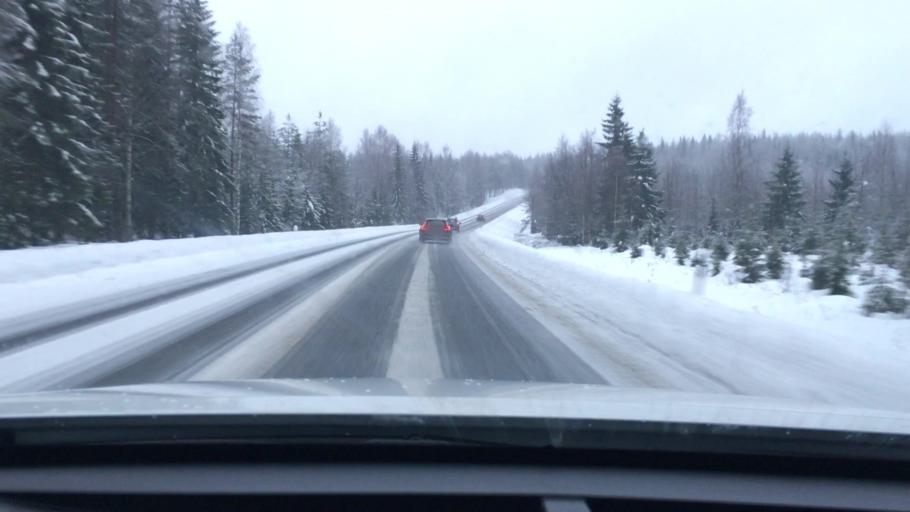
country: FI
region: Northern Savo
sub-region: Ylae-Savo
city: Sonkajaervi
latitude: 63.7703
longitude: 27.4147
